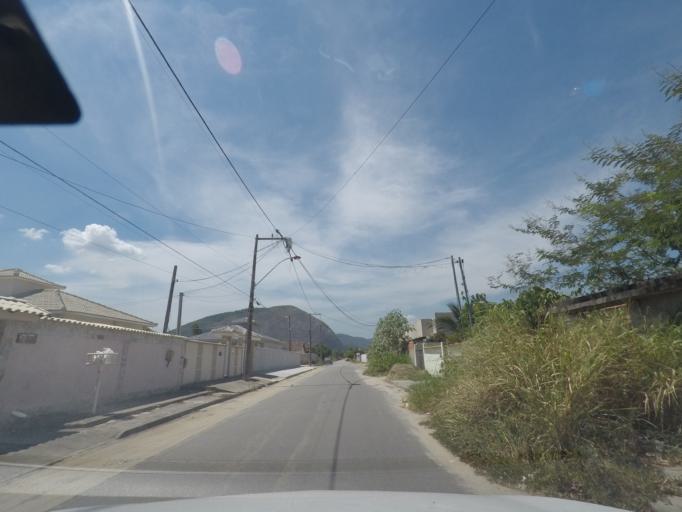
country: BR
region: Rio de Janeiro
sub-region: Marica
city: Marica
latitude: -22.9602
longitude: -42.9577
